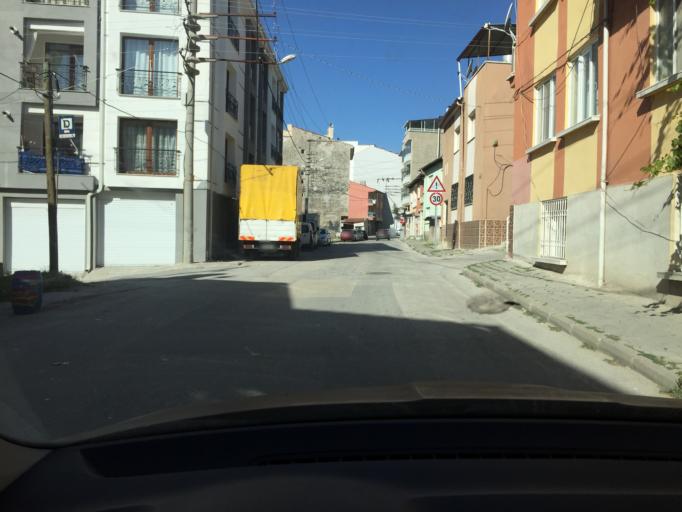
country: TR
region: Eskisehir
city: Eskisehir
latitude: 39.7765
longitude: 30.4725
